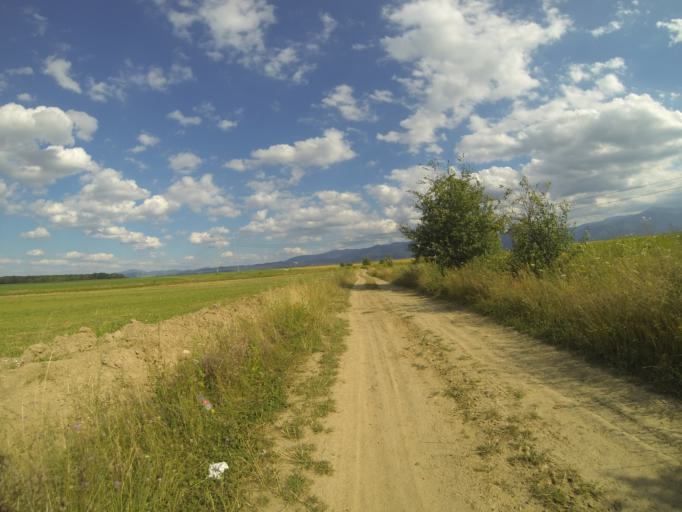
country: RO
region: Brasov
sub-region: Comuna Mandra
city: Mandra
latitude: 45.7682
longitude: 25.0742
